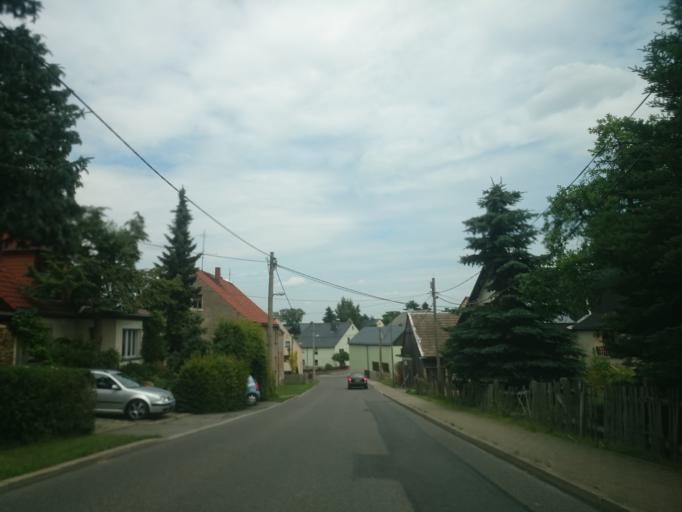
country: DE
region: Saxony
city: Eppendorf
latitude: 50.7859
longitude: 13.2279
